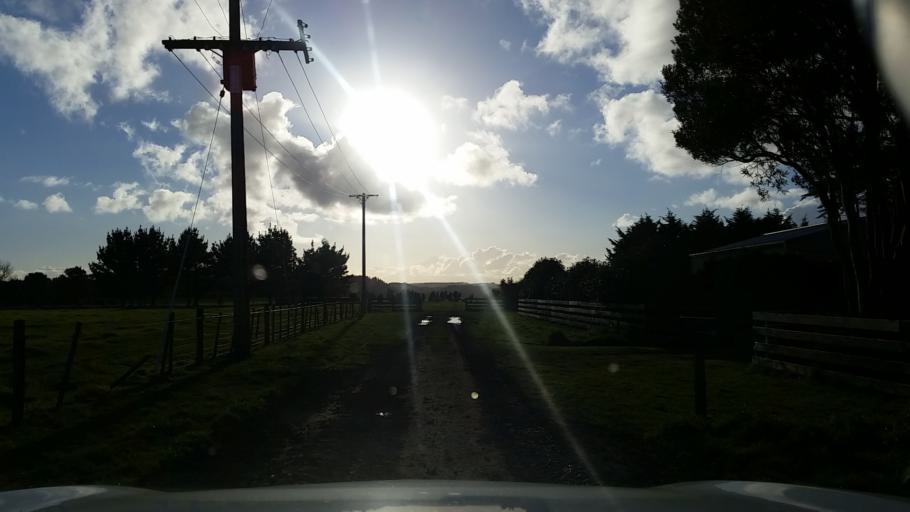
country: NZ
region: Taranaki
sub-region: South Taranaki District
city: Patea
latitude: -39.6148
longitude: 174.4928
